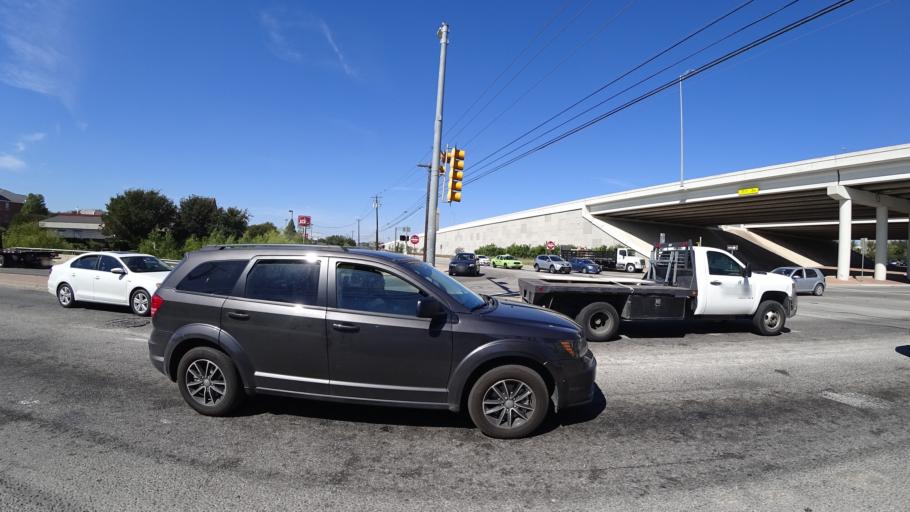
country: US
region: Texas
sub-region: Travis County
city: Austin
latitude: 30.2117
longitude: -97.7123
